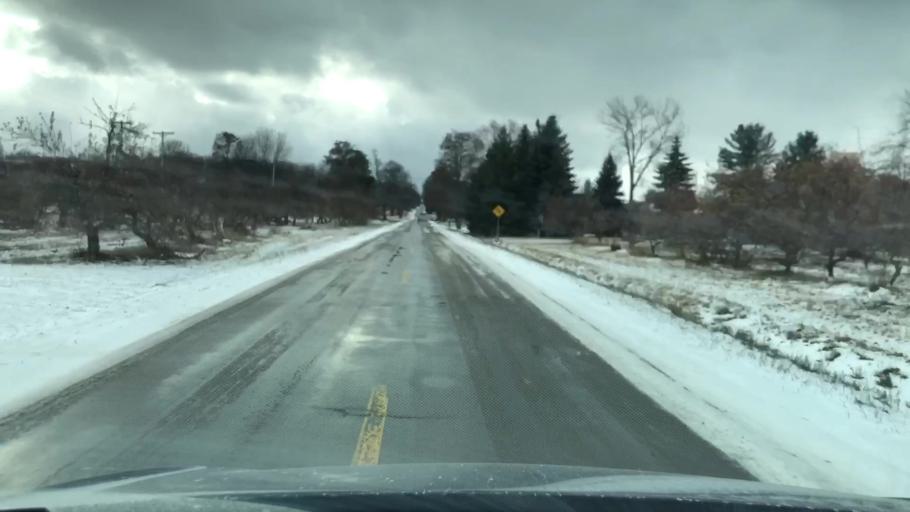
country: US
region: Michigan
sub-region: Antrim County
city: Elk Rapids
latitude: 44.9044
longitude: -85.5154
